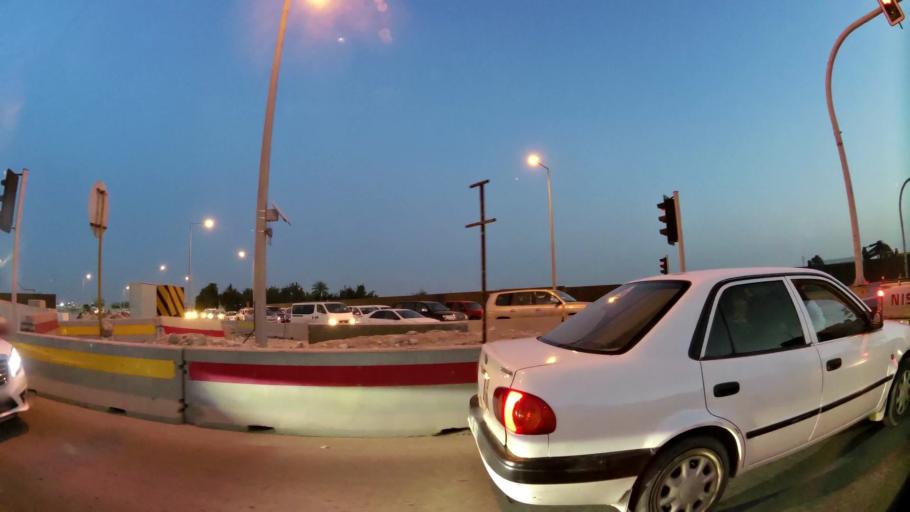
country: QA
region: Baladiyat ar Rayyan
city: Ar Rayyan
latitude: 25.3012
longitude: 51.4494
